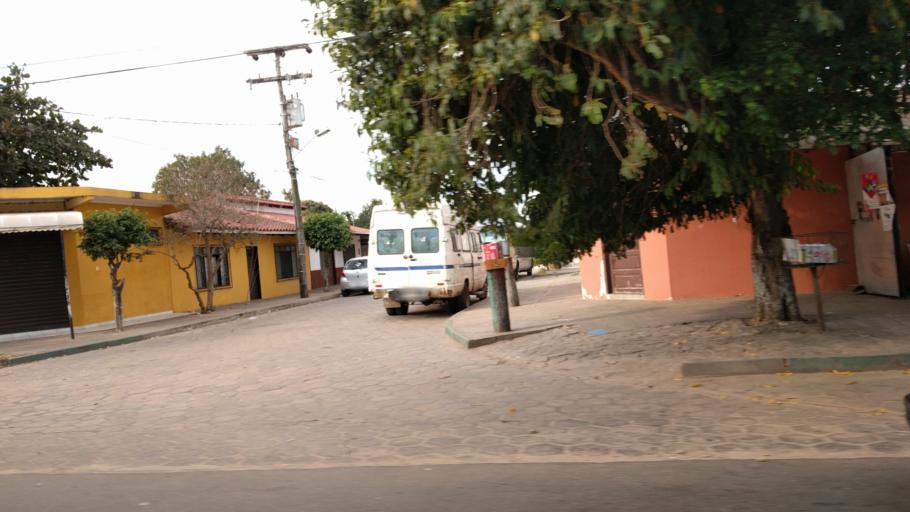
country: BO
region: Santa Cruz
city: Warnes
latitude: -17.5084
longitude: -63.1687
